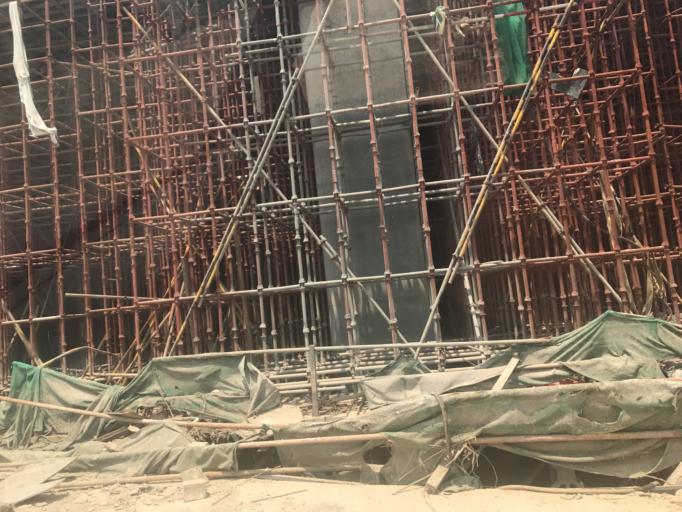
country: CN
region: Hubei
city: Zhanjiaji
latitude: 30.6848
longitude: 114.3393
